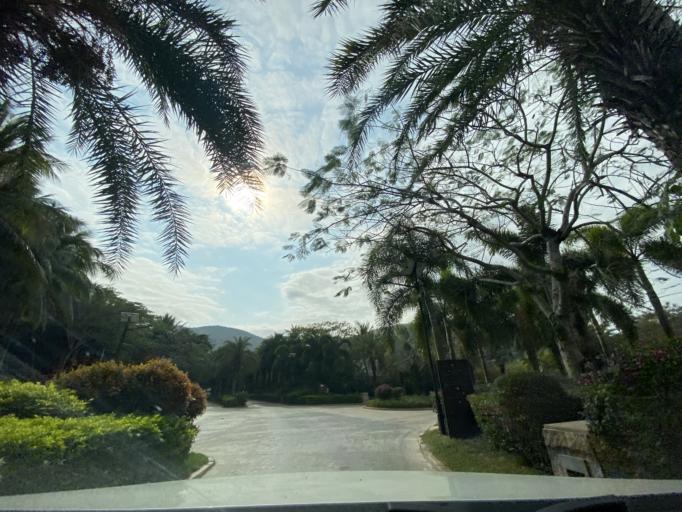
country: CN
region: Hainan
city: Tiandu
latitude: 18.2202
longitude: 109.6146
